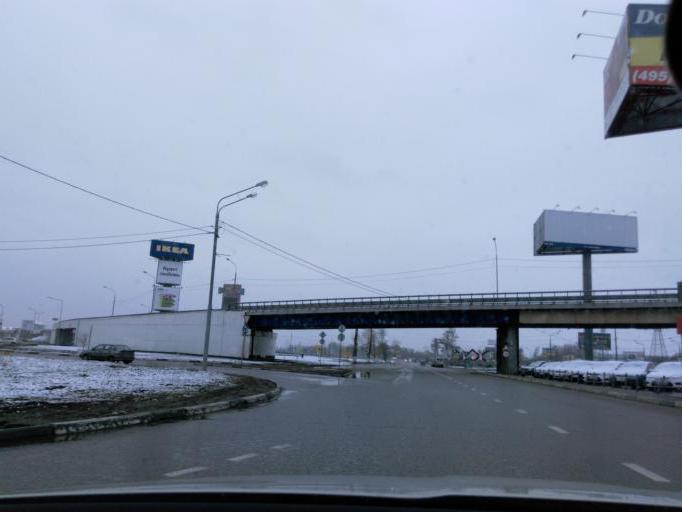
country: RU
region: Moscow
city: Khimki
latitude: 55.9108
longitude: 37.4055
